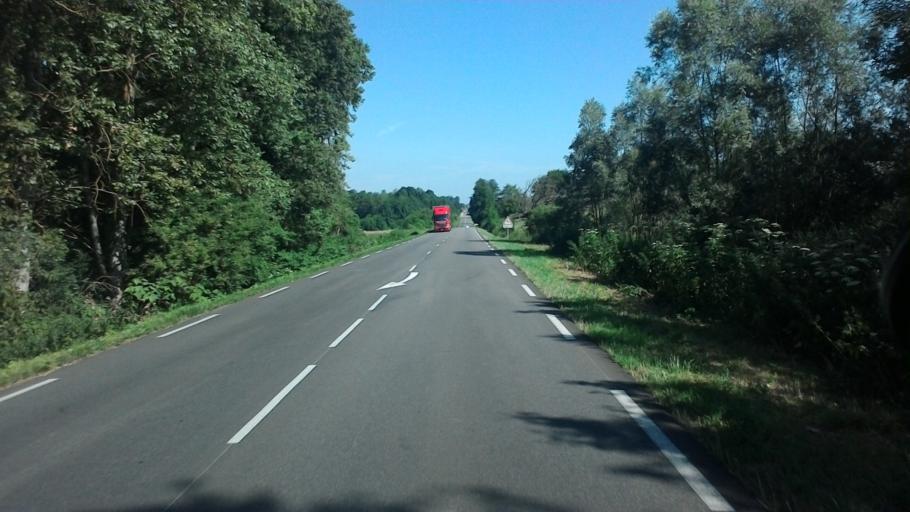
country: FR
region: Bourgogne
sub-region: Departement de Saone-et-Loire
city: Romenay
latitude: 46.4898
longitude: 5.0703
